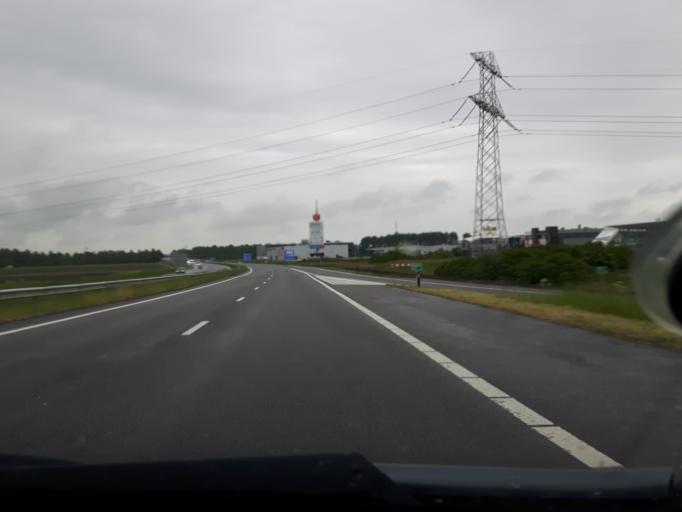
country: NL
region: Zeeland
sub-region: Gemeente Goes
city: Goes
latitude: 51.4853
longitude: 3.8707
